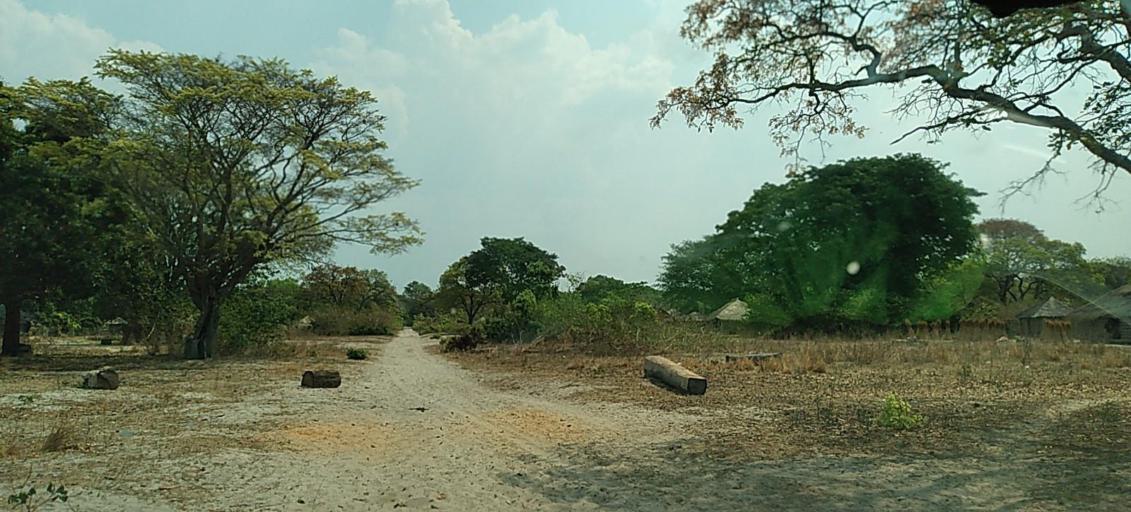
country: ZM
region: North-Western
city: Kabompo
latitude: -13.3857
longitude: 23.7674
